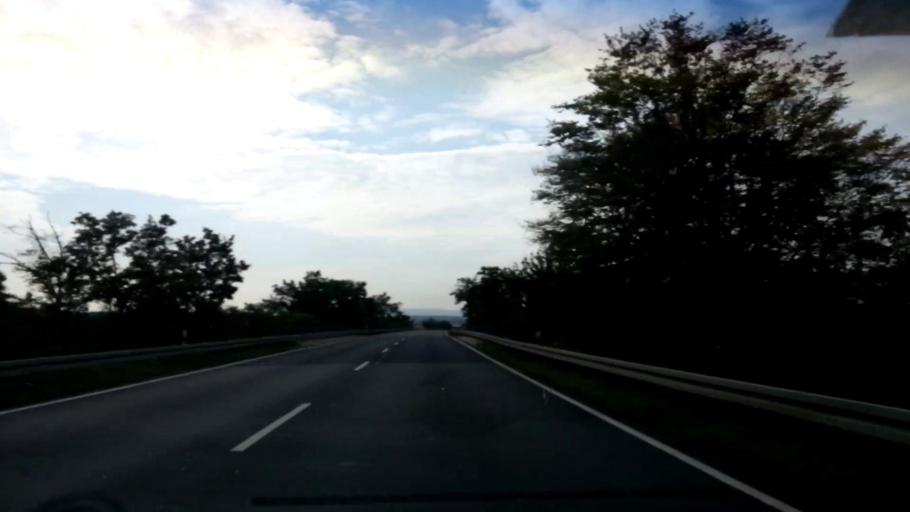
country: DE
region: Bavaria
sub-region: Regierungsbezirk Unterfranken
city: Lulsfeld
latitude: 49.8570
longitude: 10.3508
